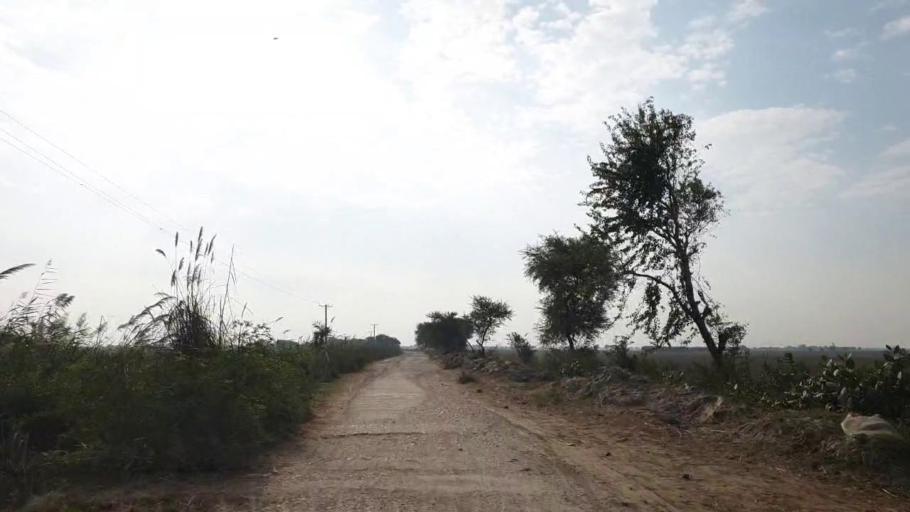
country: PK
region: Sindh
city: Tando Muhammad Khan
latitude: 25.0336
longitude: 68.4384
